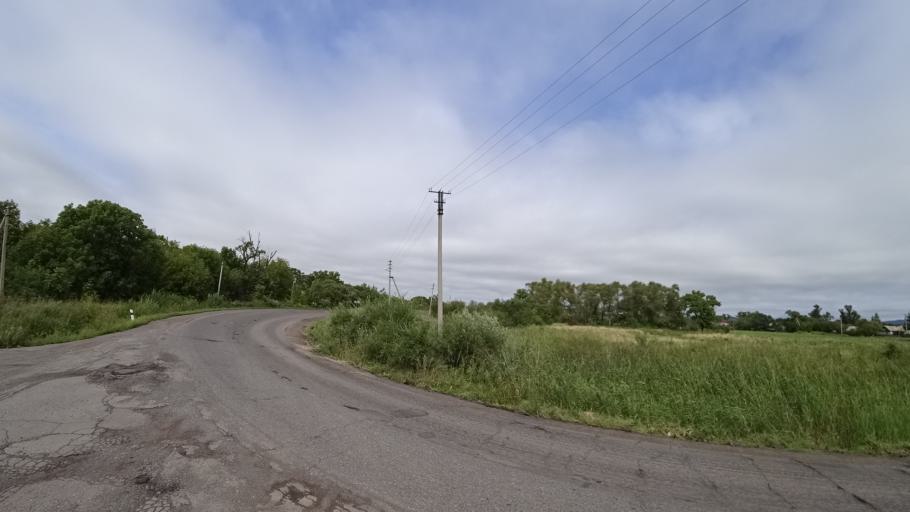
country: RU
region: Primorskiy
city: Monastyrishche
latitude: 44.1900
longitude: 132.4821
